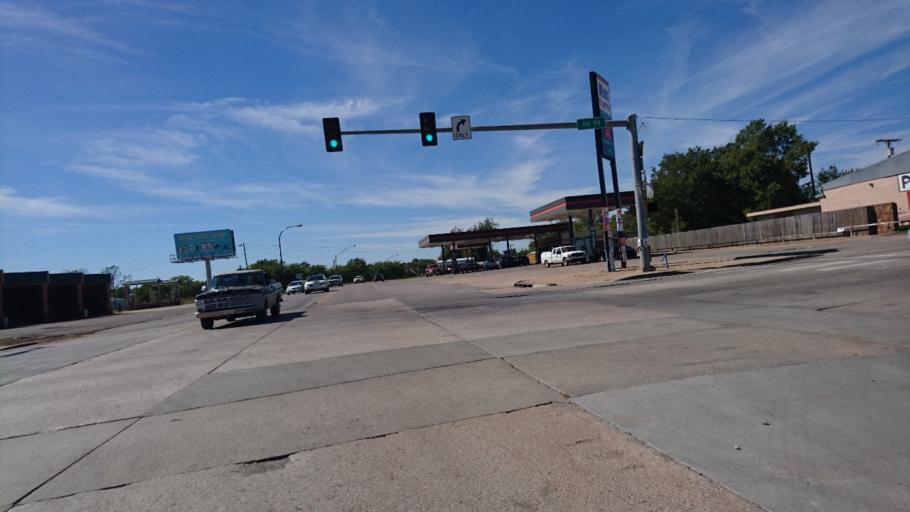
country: US
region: Oklahoma
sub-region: Lincoln County
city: Stroud
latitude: 35.7492
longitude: -96.6627
